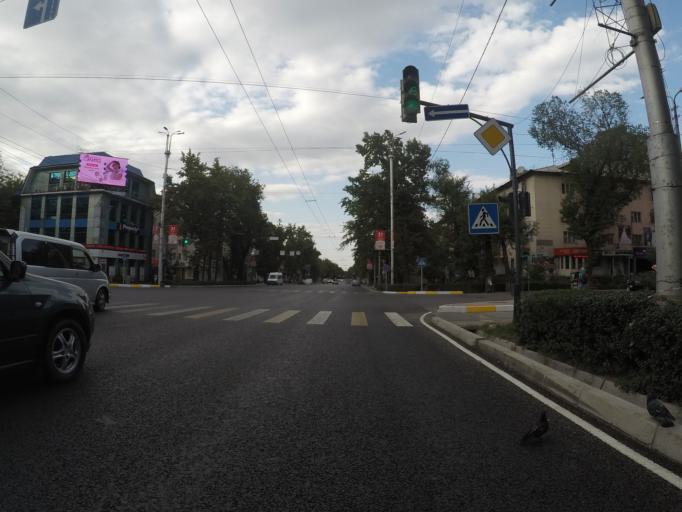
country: KG
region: Chuy
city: Bishkek
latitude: 42.8726
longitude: 74.5880
